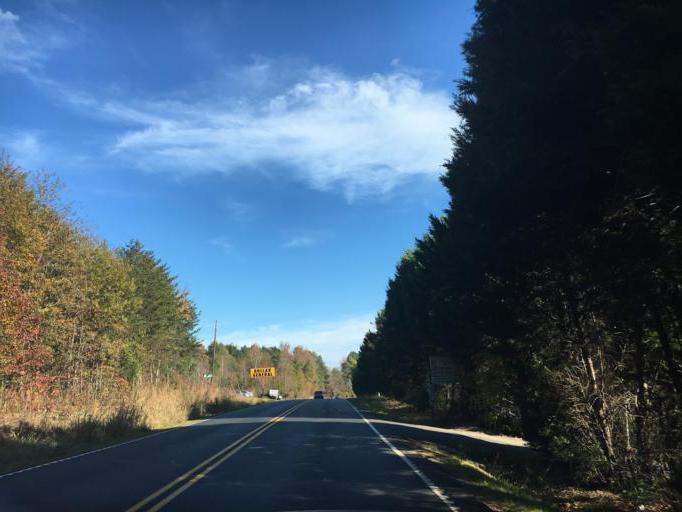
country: US
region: South Carolina
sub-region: Spartanburg County
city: Fairforest
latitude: 34.9970
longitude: -82.0528
